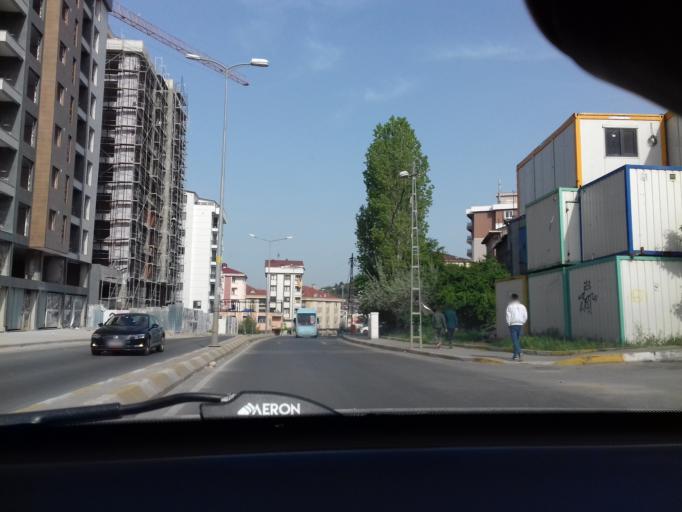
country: TR
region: Istanbul
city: Pendik
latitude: 40.9079
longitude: 29.2576
